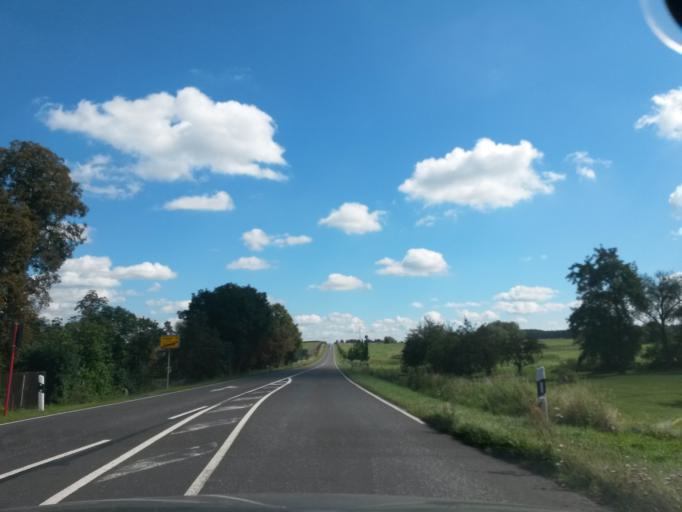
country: DE
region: Brandenburg
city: Schoneberg
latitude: 53.0314
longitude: 14.1162
